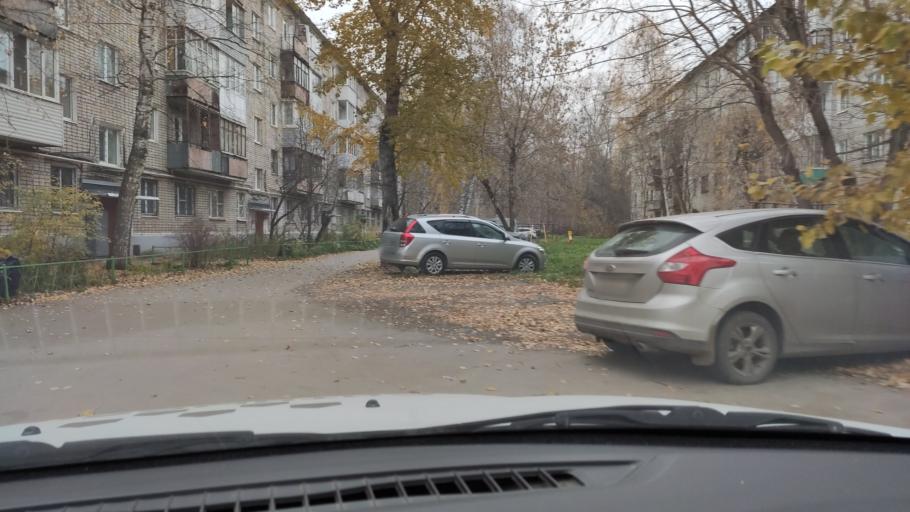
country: RU
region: Perm
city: Perm
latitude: 58.0080
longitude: 56.2730
